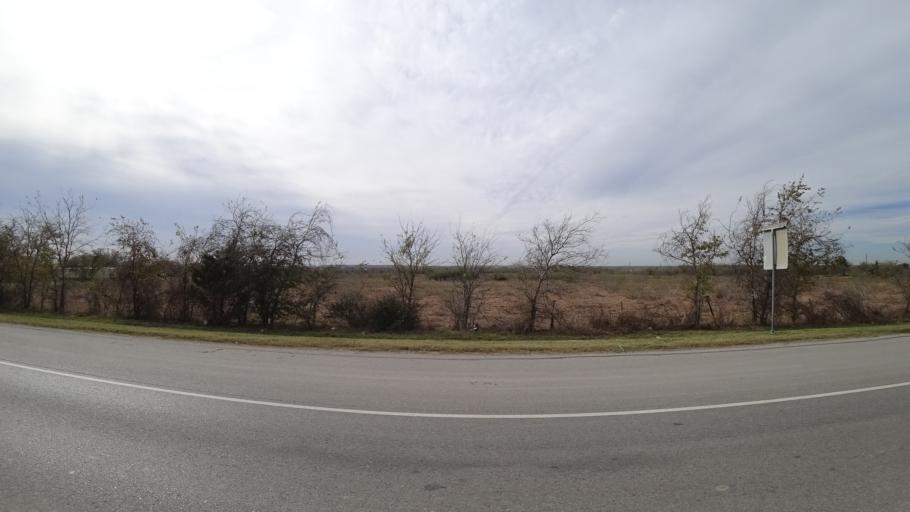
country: US
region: Texas
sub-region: Travis County
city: Garfield
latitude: 30.1232
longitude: -97.6383
